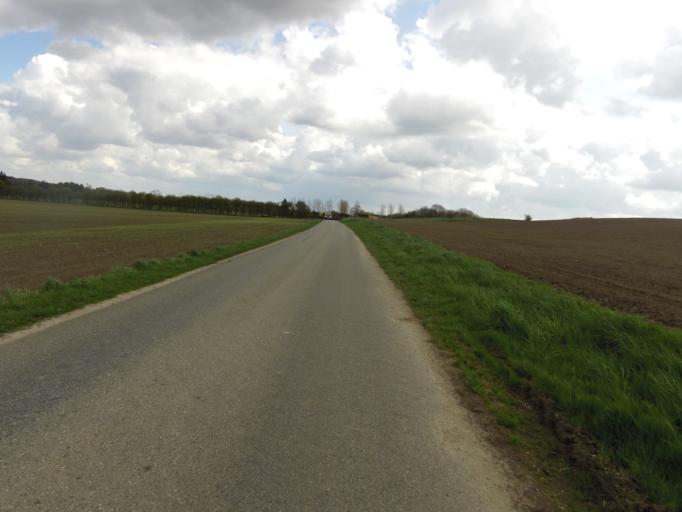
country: DK
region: South Denmark
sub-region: Tonder Kommune
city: Toftlund
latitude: 55.2135
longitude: 9.1494
